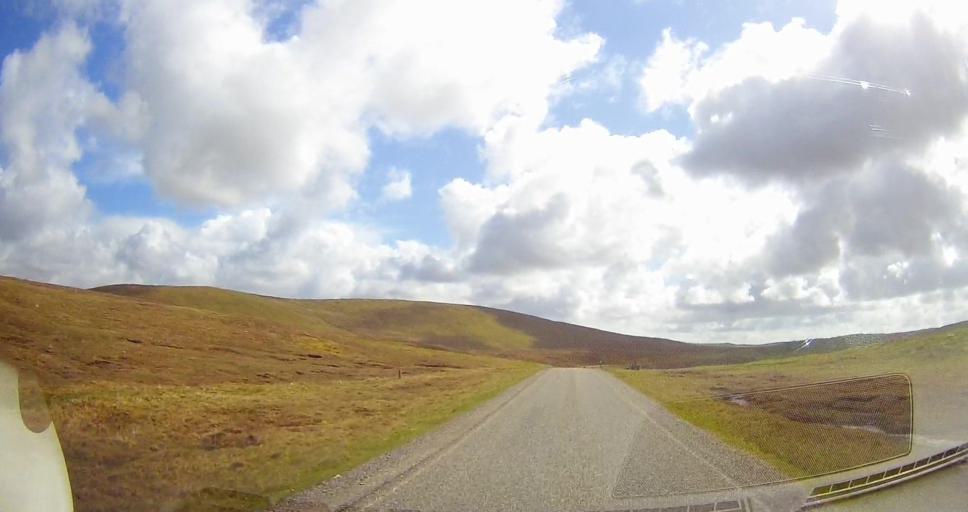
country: GB
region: Scotland
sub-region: Shetland Islands
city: Lerwick
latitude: 60.5206
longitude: -1.3772
